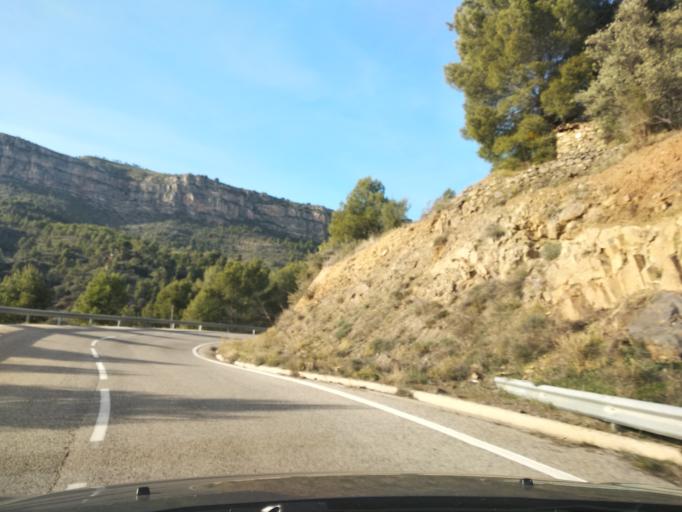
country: ES
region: Catalonia
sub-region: Provincia de Tarragona
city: Margalef
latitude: 41.2342
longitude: 0.7817
